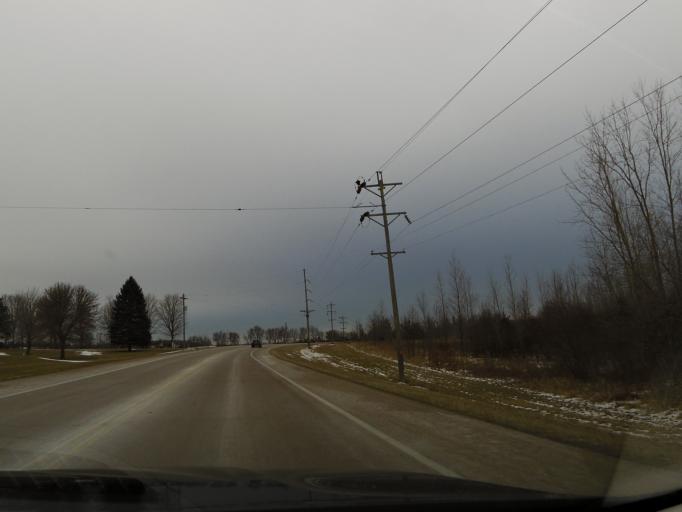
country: US
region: Minnesota
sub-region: Carver County
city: Watertown
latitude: 44.9252
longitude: -93.8294
